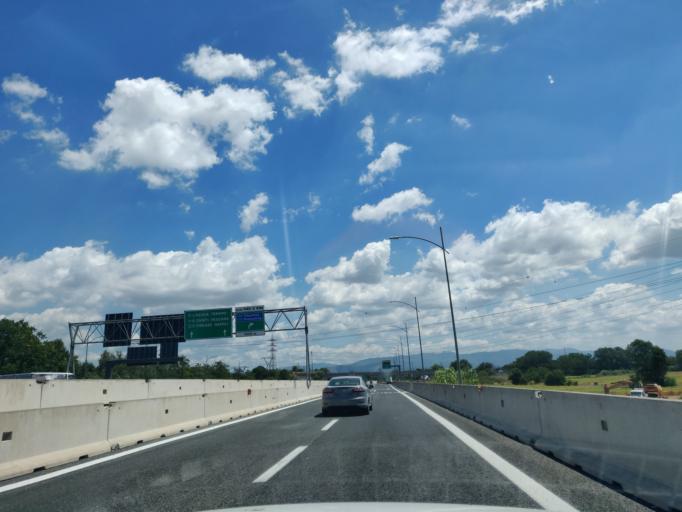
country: IT
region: Latium
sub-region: Citta metropolitana di Roma Capitale
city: Setteville
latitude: 41.9229
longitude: 12.6347
